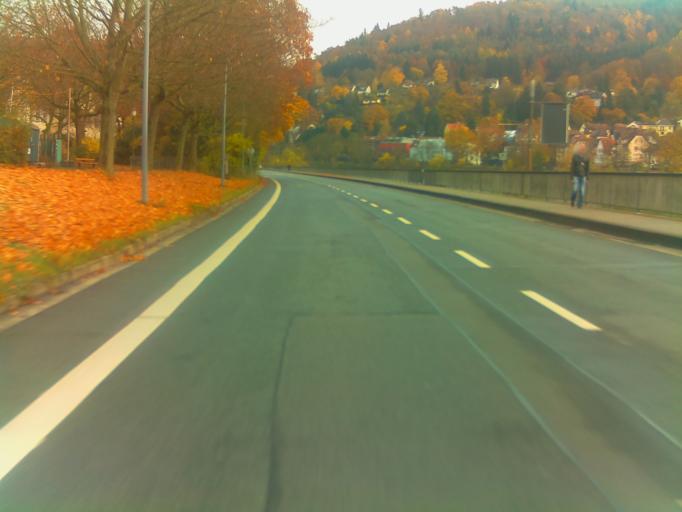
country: DE
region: Baden-Wuerttemberg
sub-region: Karlsruhe Region
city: Heidelberg
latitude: 49.4178
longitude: 8.7402
